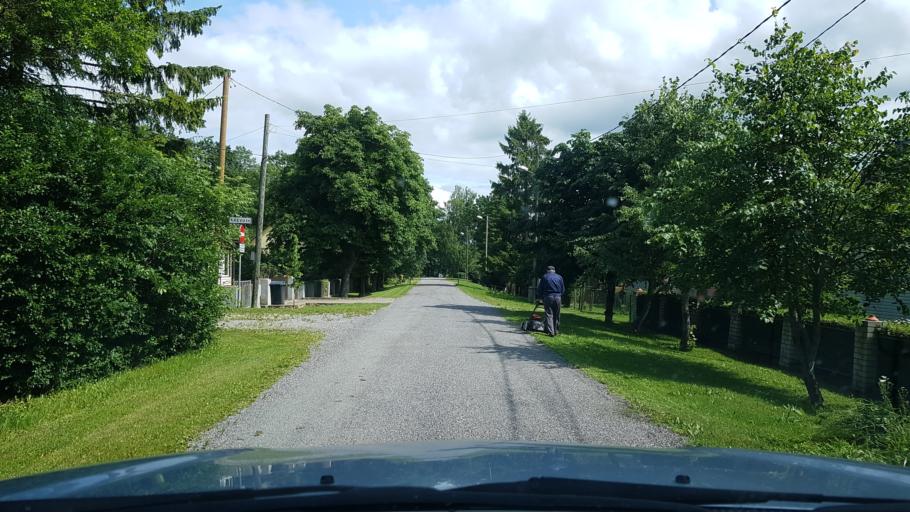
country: EE
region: Ida-Virumaa
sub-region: Sillamaee linn
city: Sillamae
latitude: 59.3728
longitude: 27.8770
